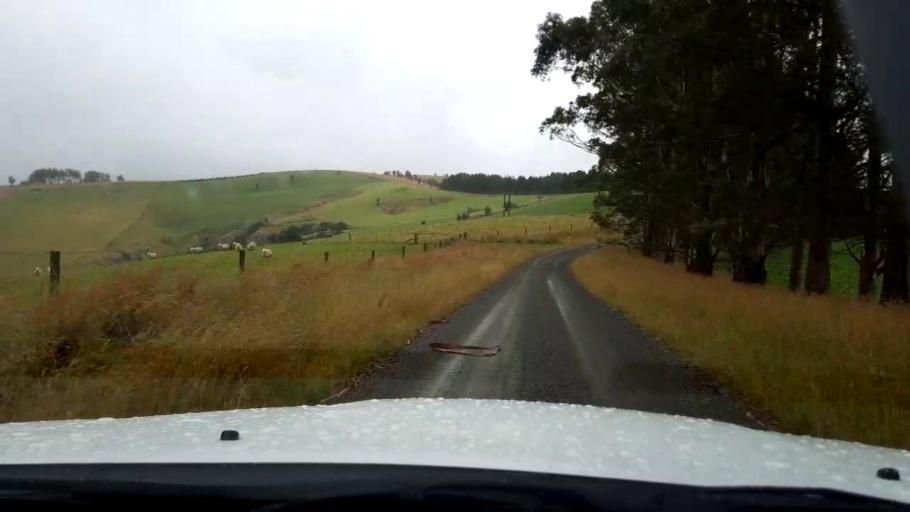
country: NZ
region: Canterbury
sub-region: Timaru District
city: Pleasant Point
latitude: -44.1731
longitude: 171.1012
